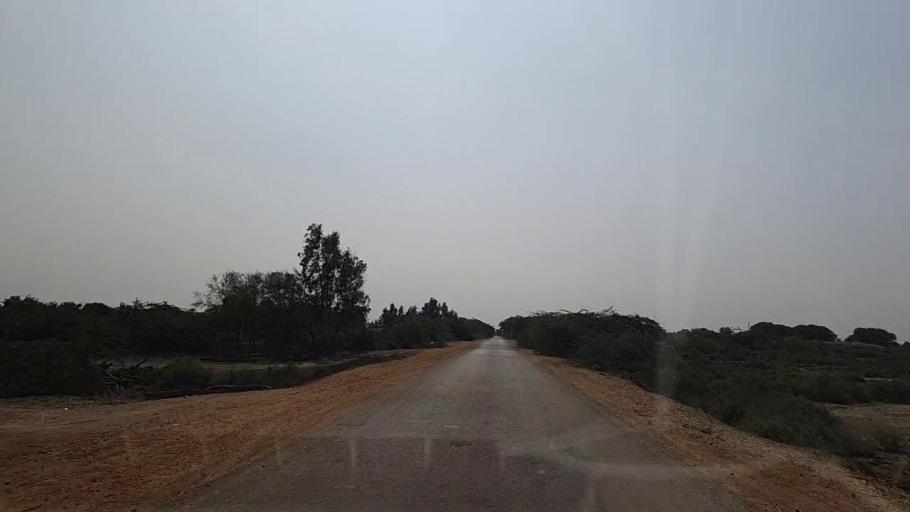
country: PK
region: Sindh
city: Chuhar Jamali
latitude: 24.2523
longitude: 67.9060
